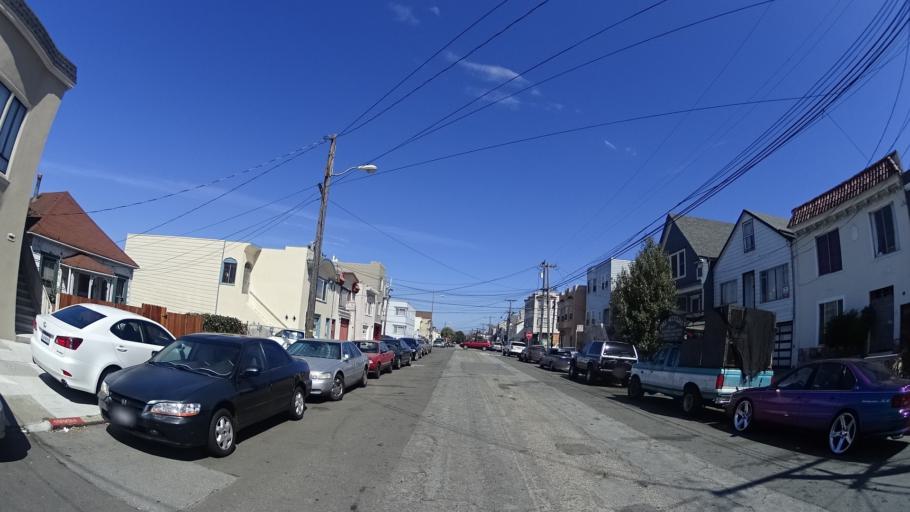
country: US
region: California
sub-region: San Mateo County
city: Daly City
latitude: 37.7235
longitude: -122.4336
